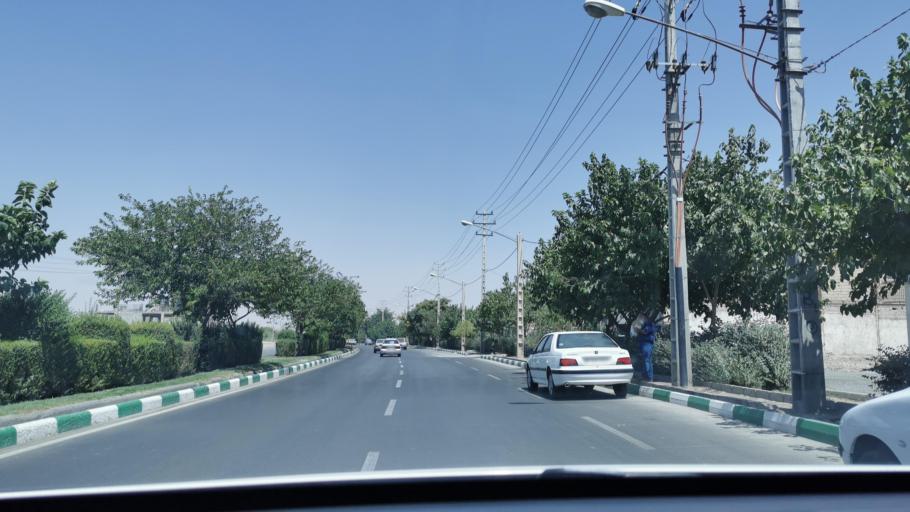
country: IR
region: Razavi Khorasan
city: Mashhad
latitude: 36.3509
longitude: 59.6298
